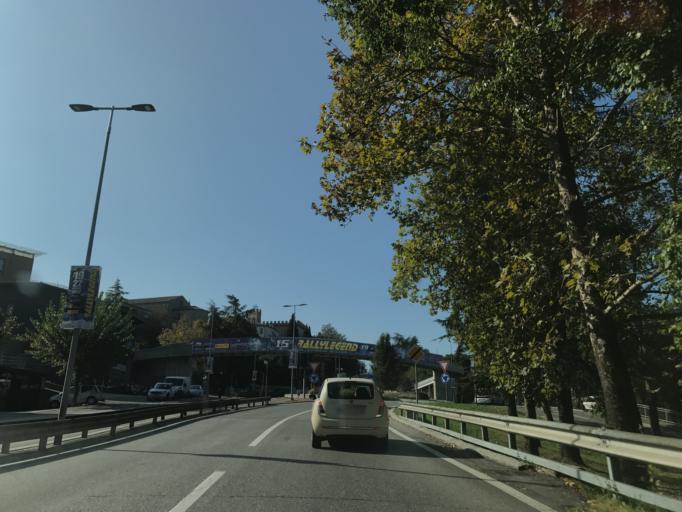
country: SM
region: Serravalle
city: Serravalle
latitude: 43.9705
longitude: 12.4797
